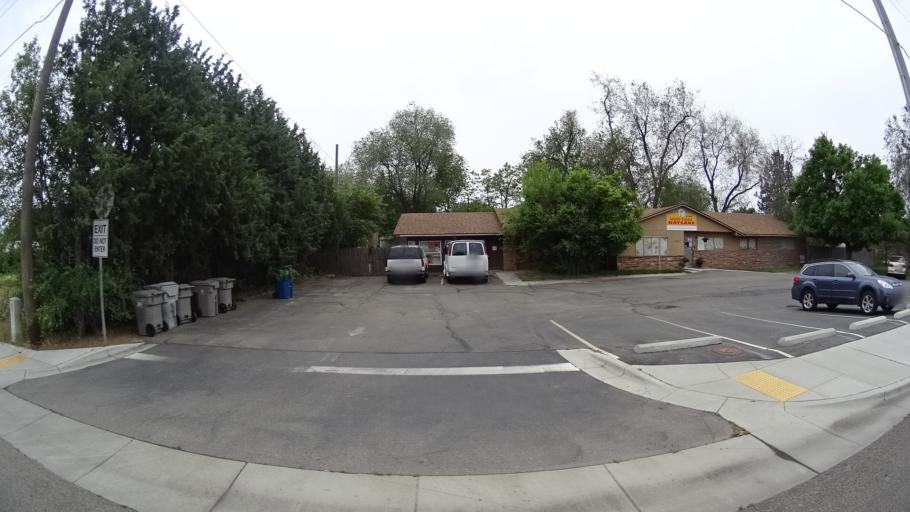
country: US
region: Idaho
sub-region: Ada County
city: Meridian
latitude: 43.6338
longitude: -116.3304
